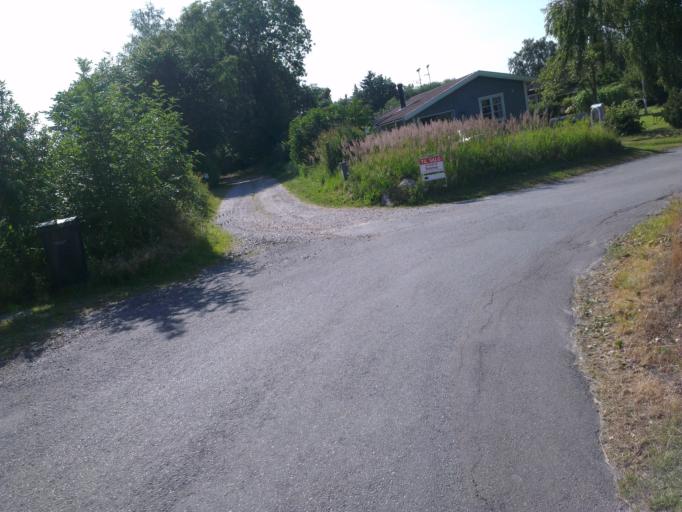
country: DK
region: Capital Region
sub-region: Halsnaes Kommune
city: Hundested
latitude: 55.9330
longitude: 11.9280
